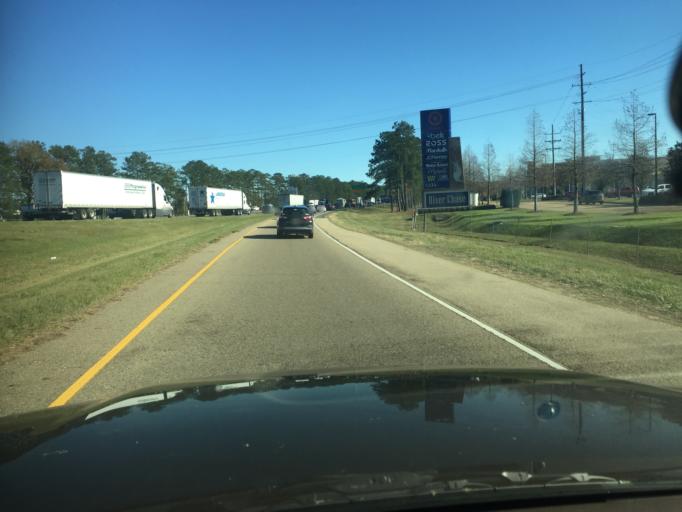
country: US
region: Louisiana
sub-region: Saint Tammany Parish
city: Covington
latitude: 30.4457
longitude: -90.1381
